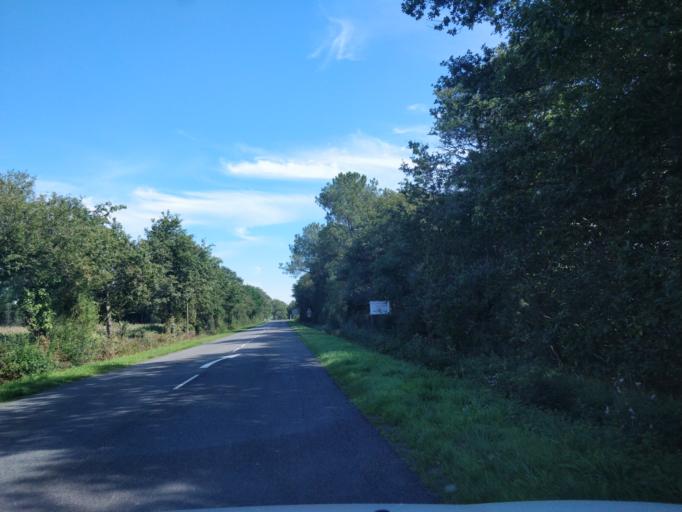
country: FR
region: Pays de la Loire
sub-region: Departement de la Loire-Atlantique
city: Quilly
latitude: 47.4789
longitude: -1.9164
